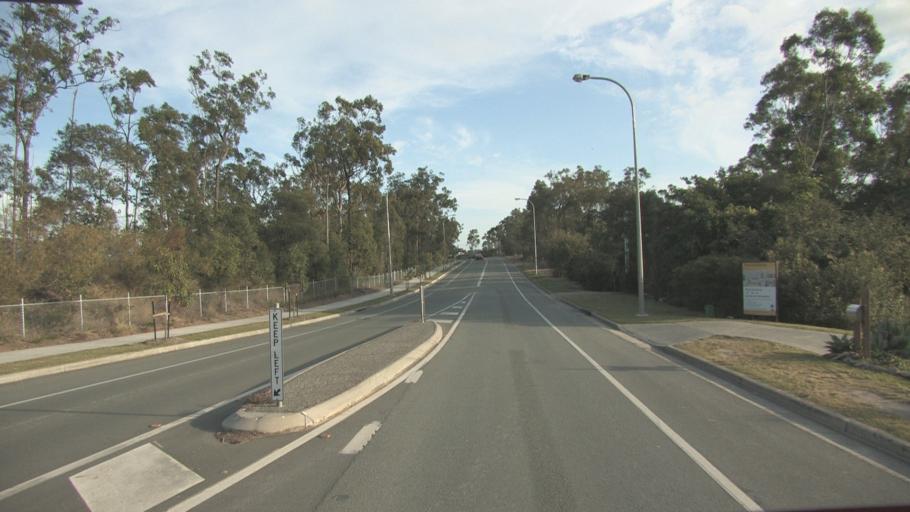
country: AU
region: Queensland
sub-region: Logan
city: Waterford West
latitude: -27.7151
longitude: 153.1588
